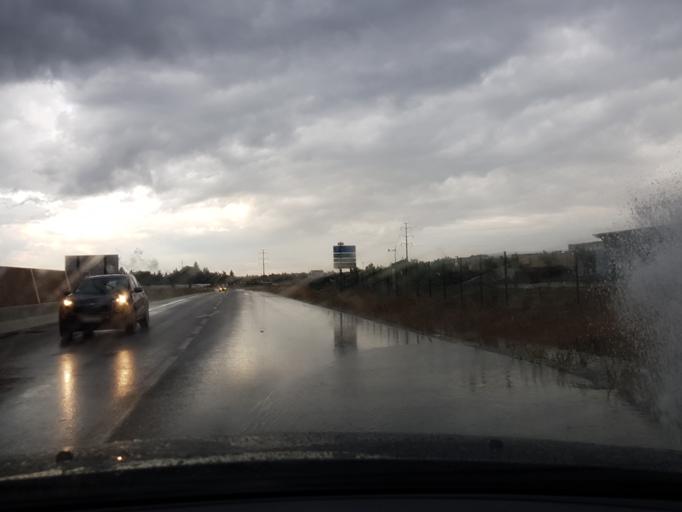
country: FR
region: Provence-Alpes-Cote d'Azur
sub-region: Departement du Vaucluse
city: Carpentras
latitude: 44.0341
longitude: 5.0368
